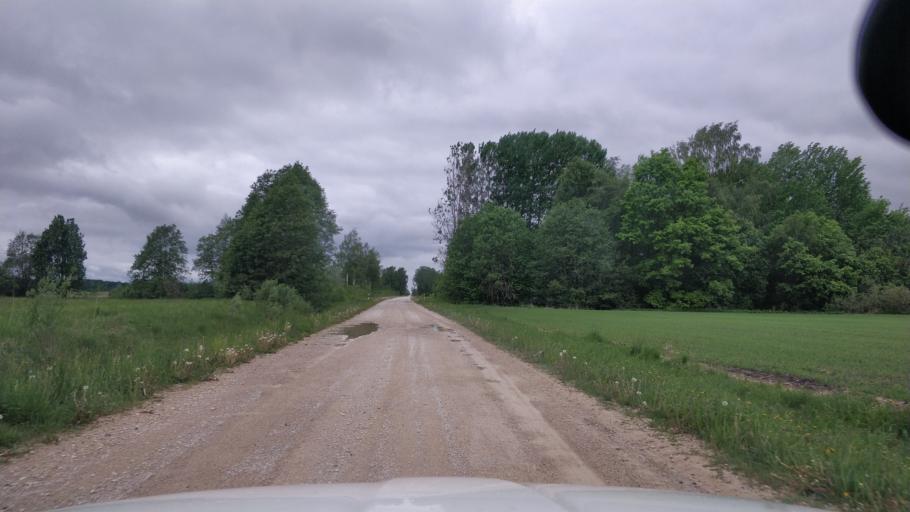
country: EE
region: Raplamaa
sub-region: Maerjamaa vald
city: Marjamaa
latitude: 58.7166
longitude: 24.2794
